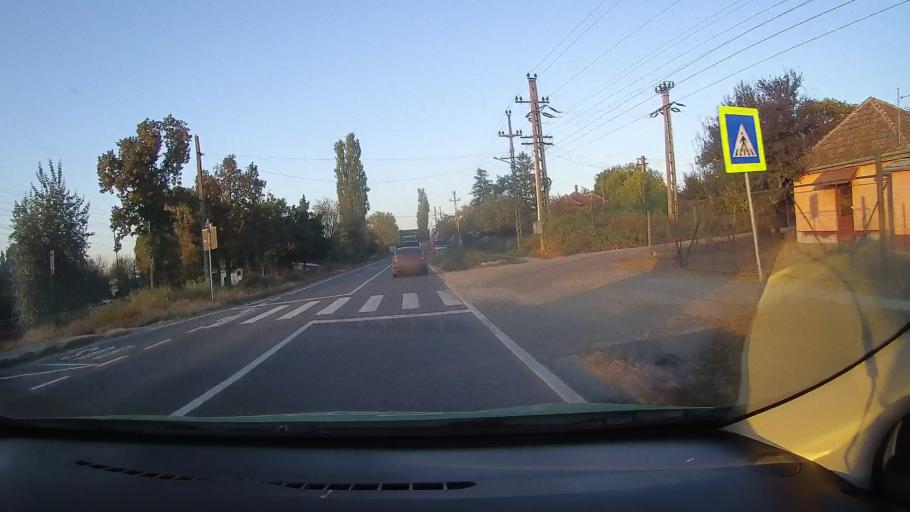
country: RO
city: Dioszeg
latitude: 47.2959
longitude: 22.0125
